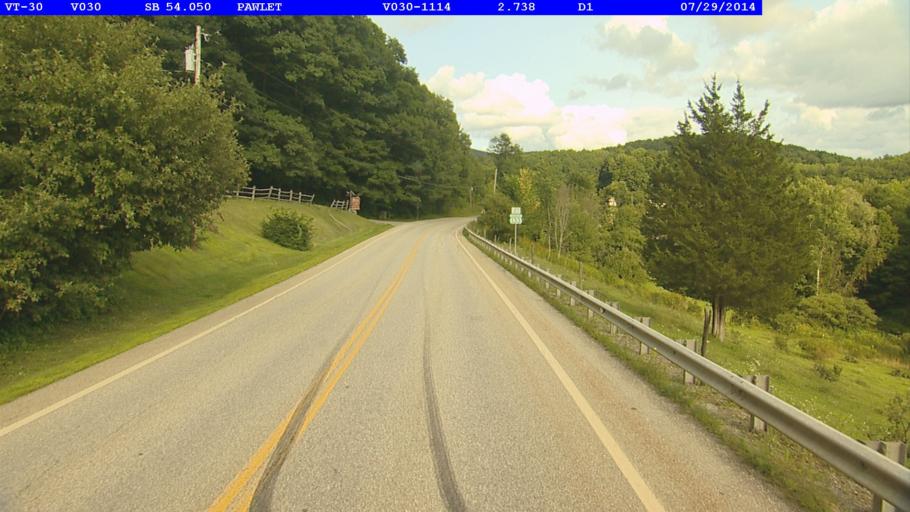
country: US
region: New York
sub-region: Washington County
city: Granville
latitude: 43.3476
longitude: -73.1810
